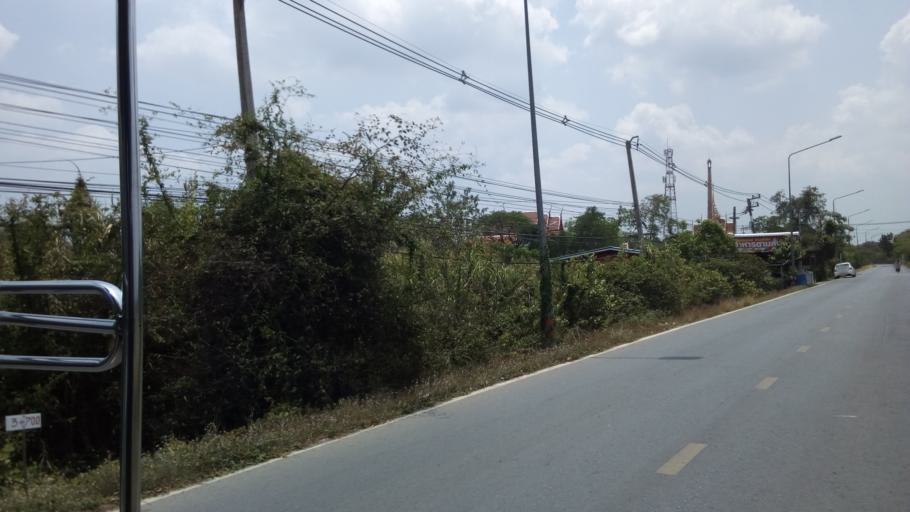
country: TH
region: Pathum Thani
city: Sam Khok
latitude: 14.0885
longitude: 100.5249
